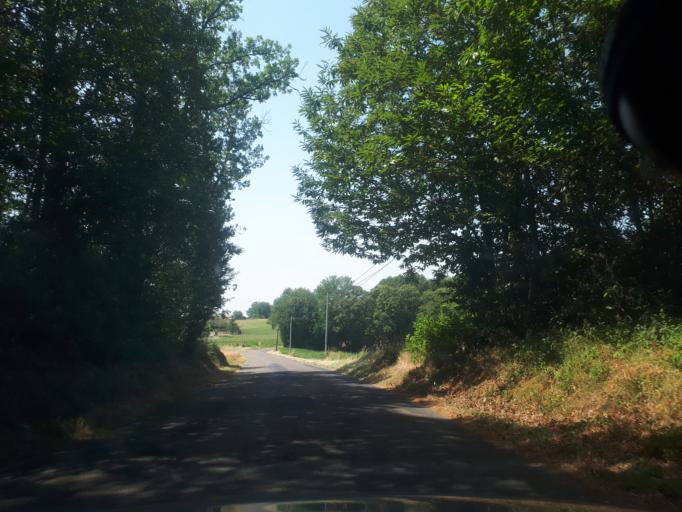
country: FR
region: Midi-Pyrenees
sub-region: Departement du Lot
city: Gourdon
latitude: 44.8277
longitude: 1.3826
